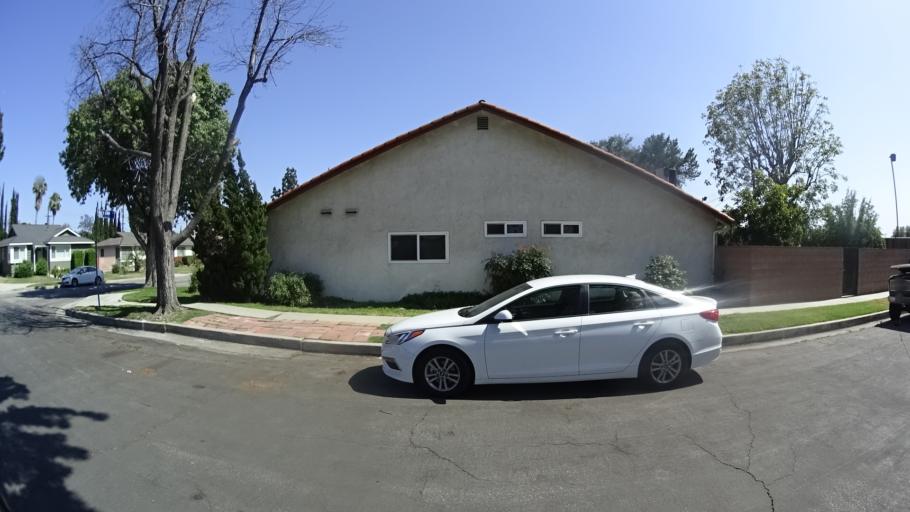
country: US
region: California
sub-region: Los Angeles County
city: Van Nuys
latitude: 34.2207
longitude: -118.4205
